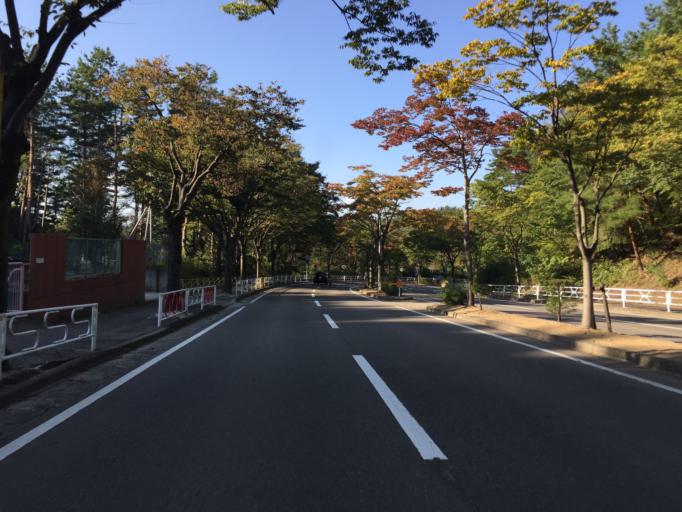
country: JP
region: Fukushima
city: Fukushima-shi
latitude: 37.7003
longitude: 140.4710
